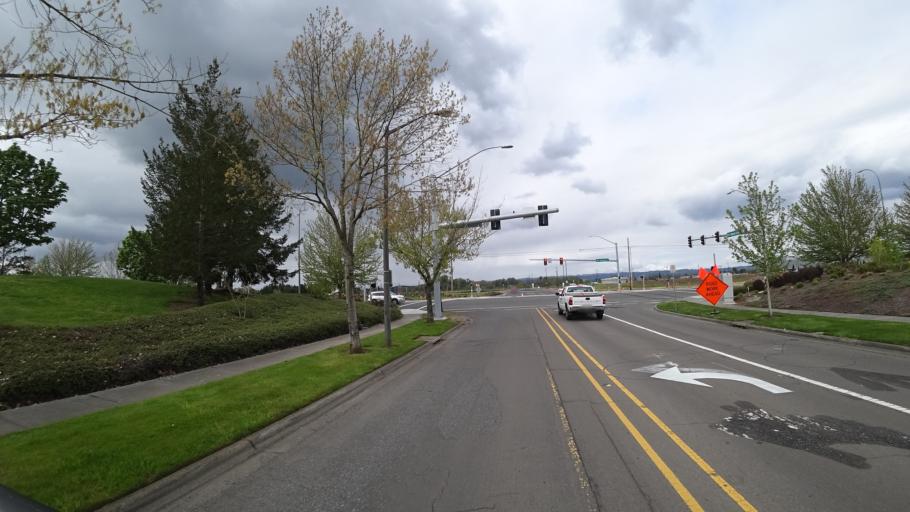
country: US
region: Oregon
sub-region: Washington County
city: Rockcreek
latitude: 45.5506
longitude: -122.9334
